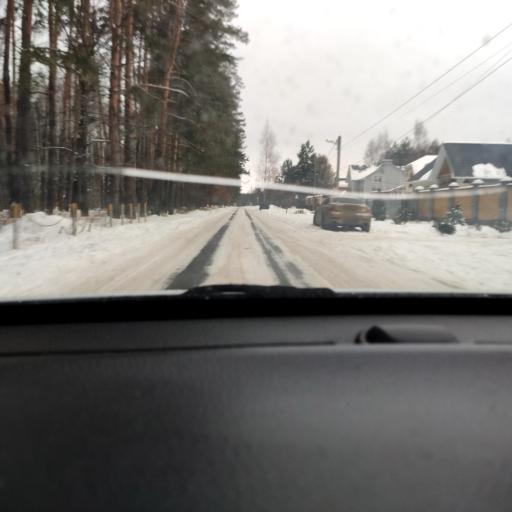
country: RU
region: Voronezj
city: Somovo
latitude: 51.7098
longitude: 39.3202
